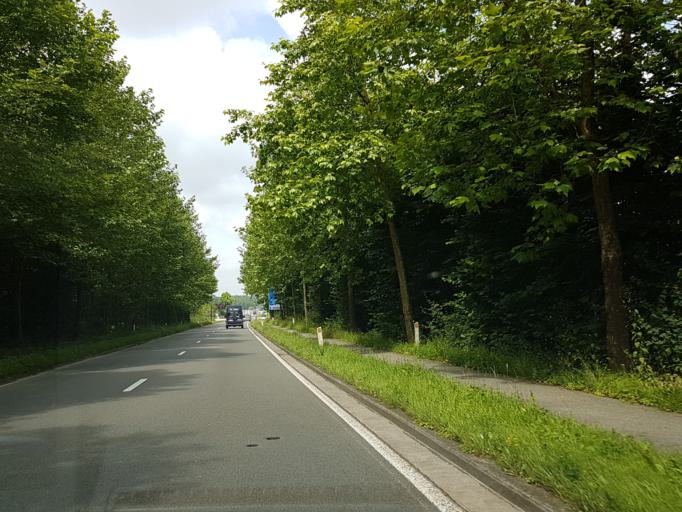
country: BE
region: Flanders
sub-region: Provincie Vlaams-Brabant
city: Liedekerke
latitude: 50.8836
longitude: 4.1007
